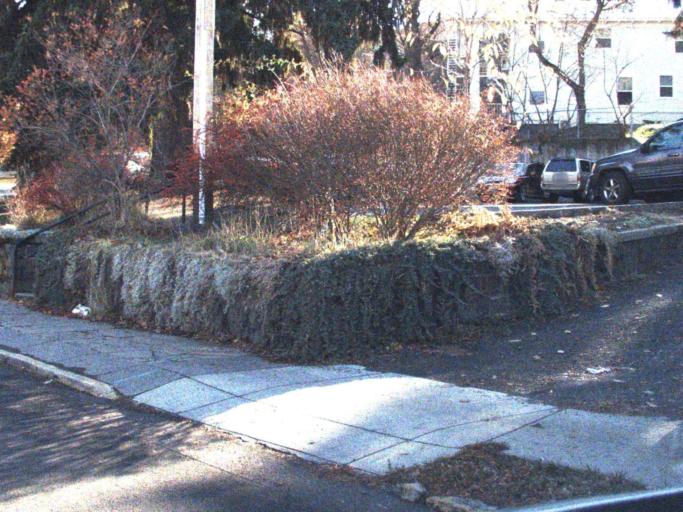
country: US
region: Washington
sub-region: Whitman County
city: Pullman
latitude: 46.7288
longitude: -117.1783
